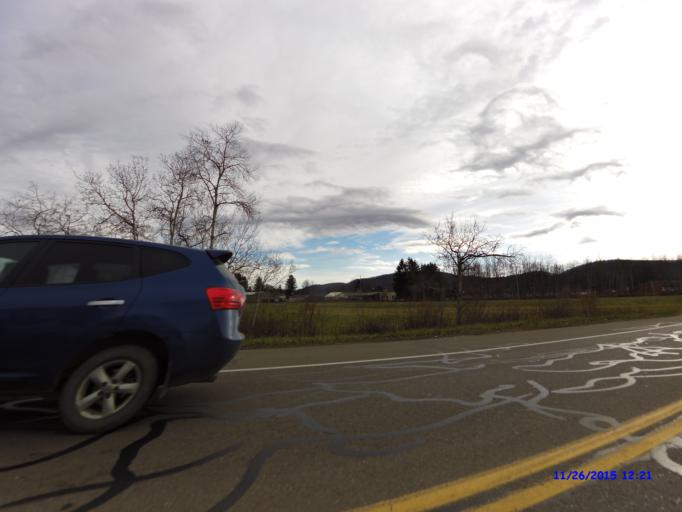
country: US
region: New York
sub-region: Cattaraugus County
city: Olean
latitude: 42.0847
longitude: -78.4494
